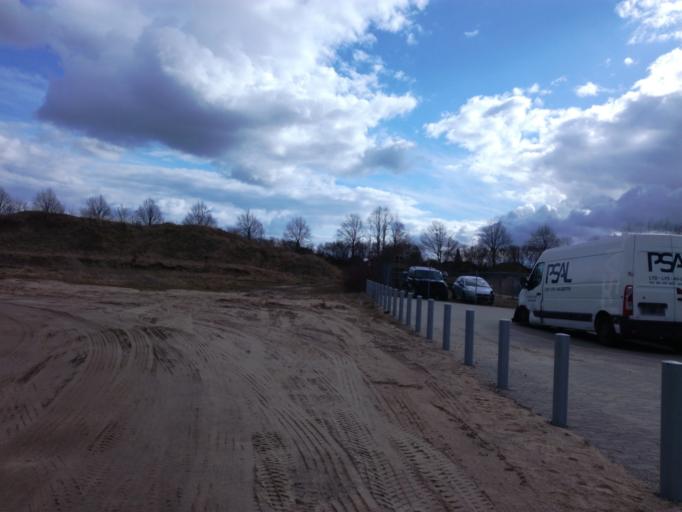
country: DK
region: South Denmark
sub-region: Fredericia Kommune
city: Fredericia
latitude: 55.5683
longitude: 9.7152
